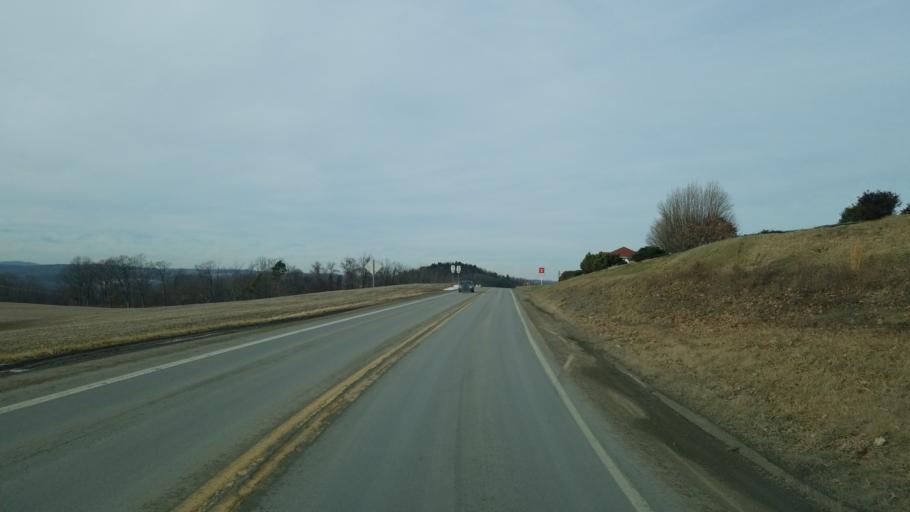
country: US
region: Pennsylvania
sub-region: Jefferson County
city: Punxsutawney
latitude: 40.9193
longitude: -78.9877
